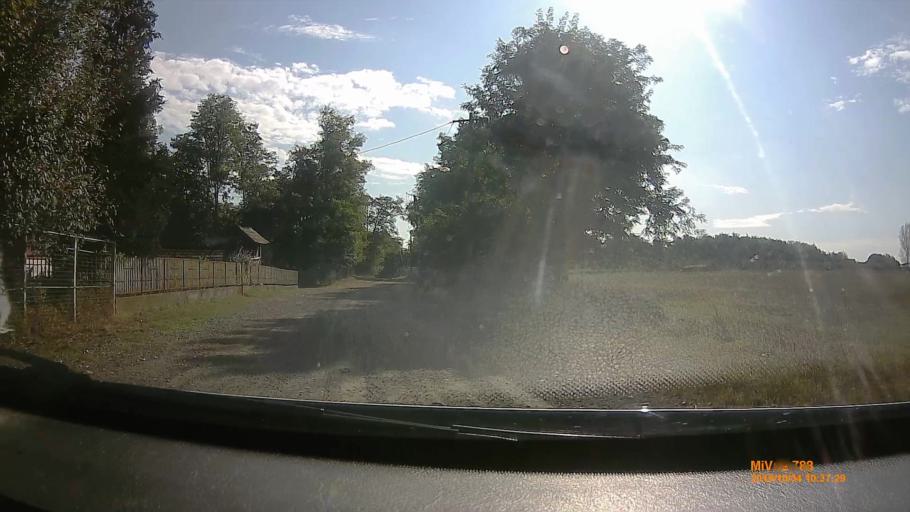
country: HU
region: Szabolcs-Szatmar-Bereg
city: Nyirtelek
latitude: 47.9738
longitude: 21.6625
